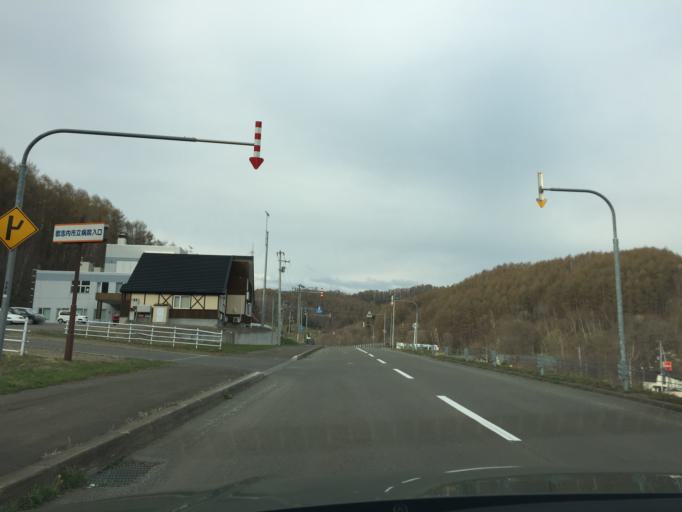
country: JP
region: Hokkaido
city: Utashinai
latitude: 43.5098
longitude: 142.0236
